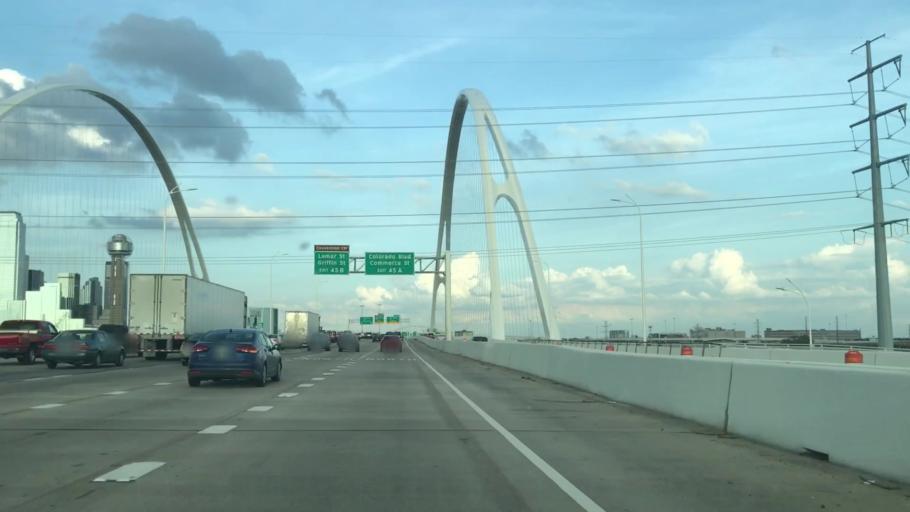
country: US
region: Texas
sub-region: Dallas County
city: Dallas
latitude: 32.7693
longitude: -96.8211
